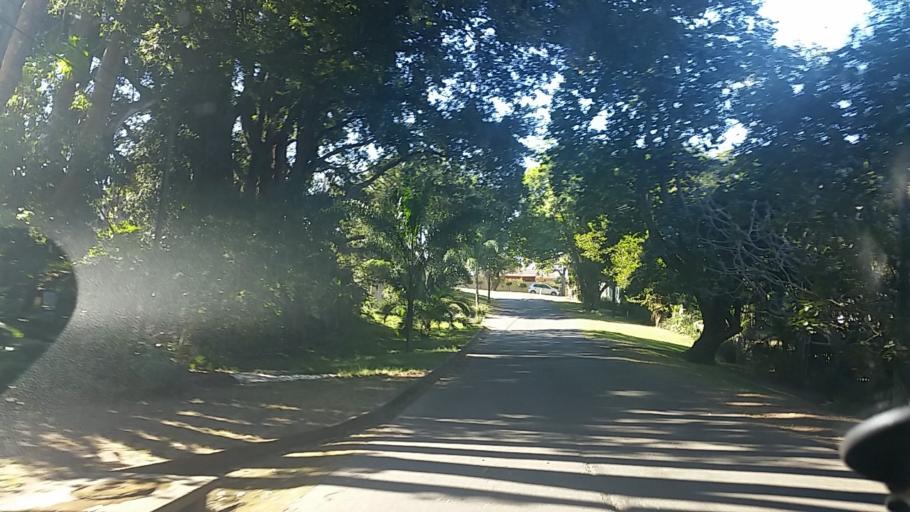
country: ZA
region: KwaZulu-Natal
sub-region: eThekwini Metropolitan Municipality
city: Berea
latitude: -29.8440
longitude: 30.9034
